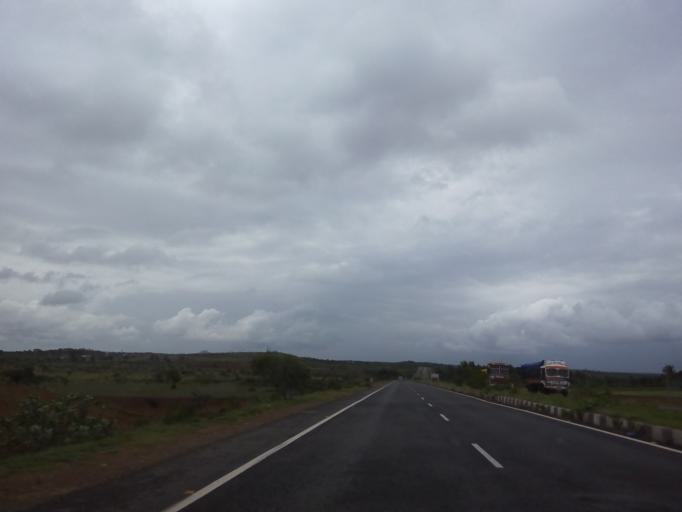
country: IN
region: Karnataka
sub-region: Haveri
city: Ranibennur
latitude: 14.5903
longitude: 75.6518
